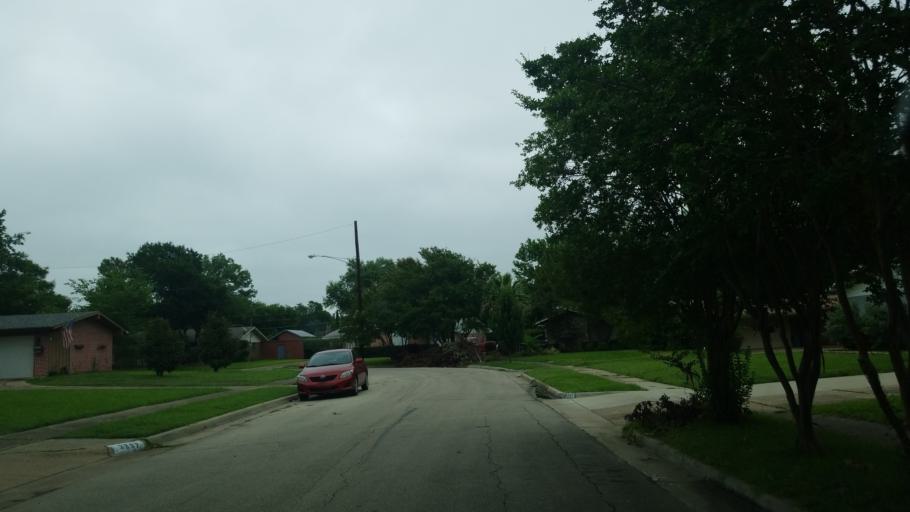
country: US
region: Texas
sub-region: Dallas County
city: Farmers Branch
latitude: 32.9057
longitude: -96.8691
